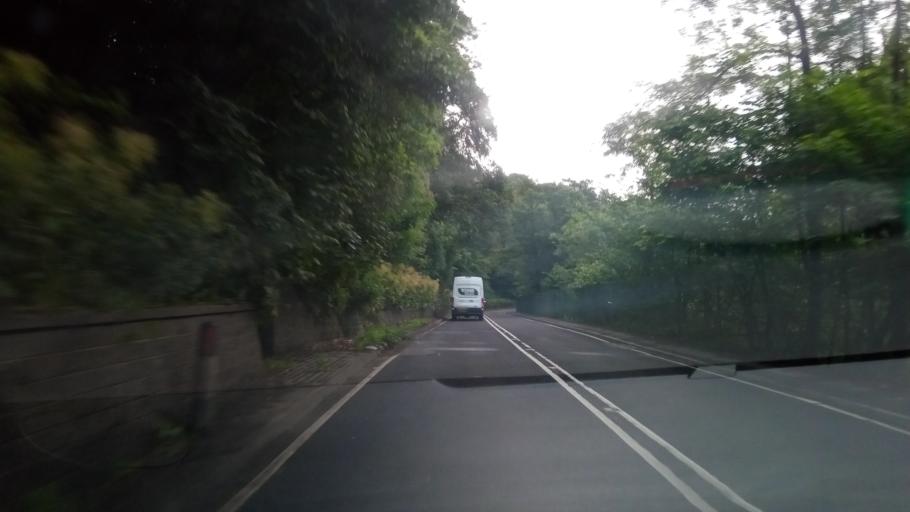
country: GB
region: Scotland
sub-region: The Scottish Borders
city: Hawick
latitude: 55.4166
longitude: -2.8041
